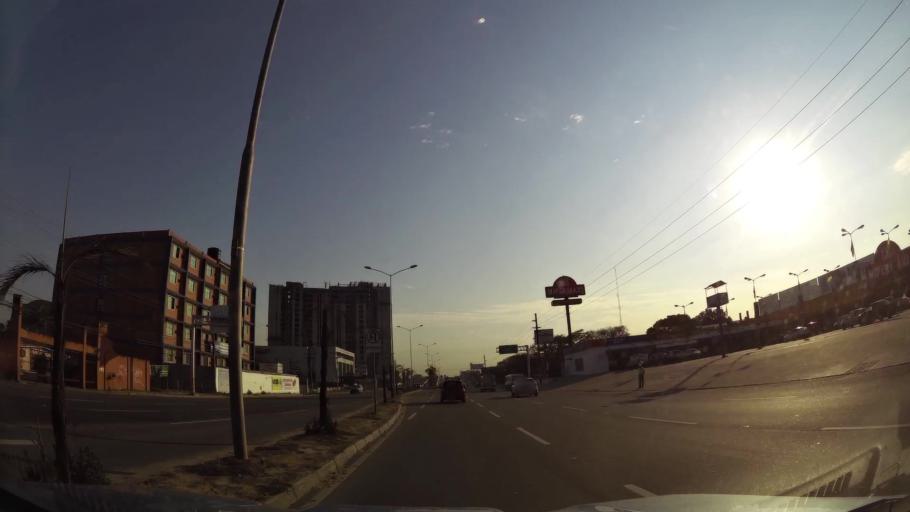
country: BO
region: Santa Cruz
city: Santa Cruz de la Sierra
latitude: -17.7288
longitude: -63.1669
